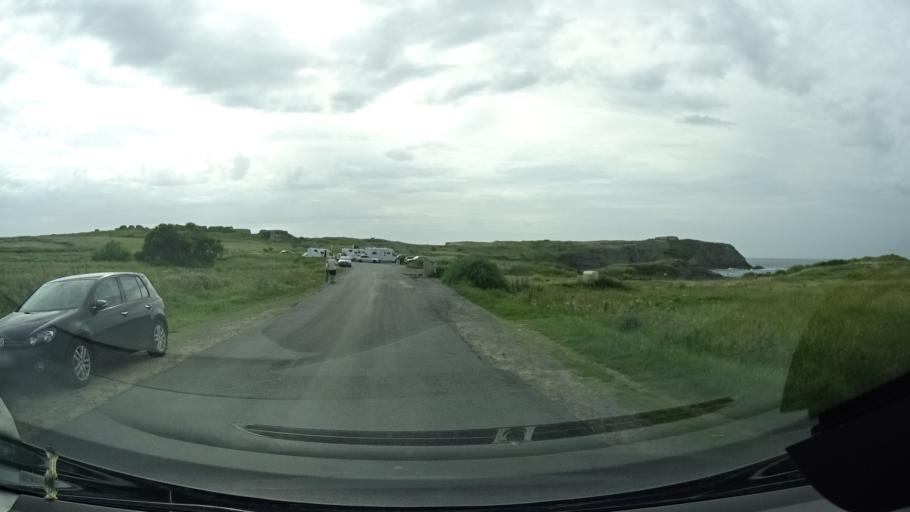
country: FR
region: Brittany
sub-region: Departement d'Ille-et-Vilaine
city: Saint-Malo
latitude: 48.6807
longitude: -1.9834
